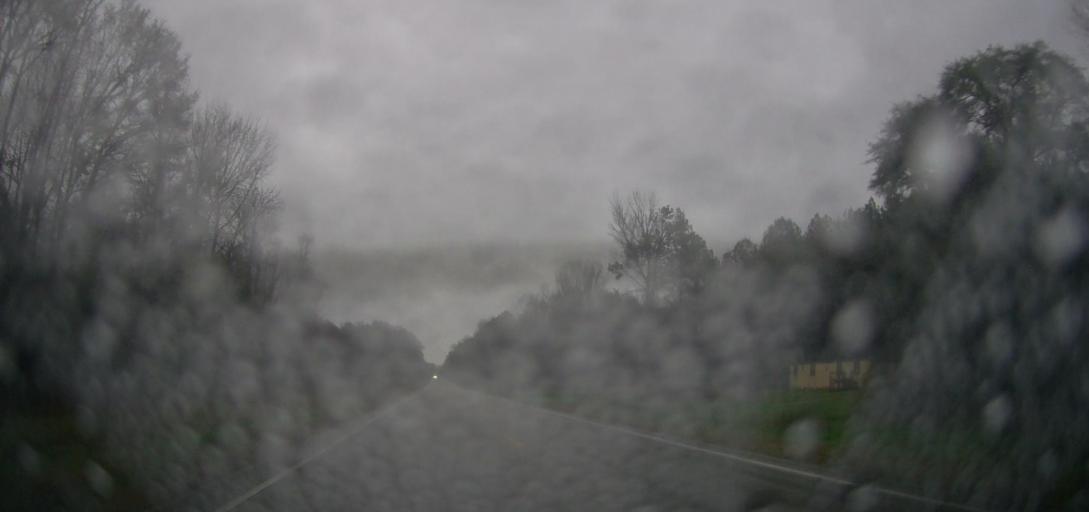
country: US
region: Alabama
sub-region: Autauga County
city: Prattville
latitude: 32.4902
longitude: -86.5621
